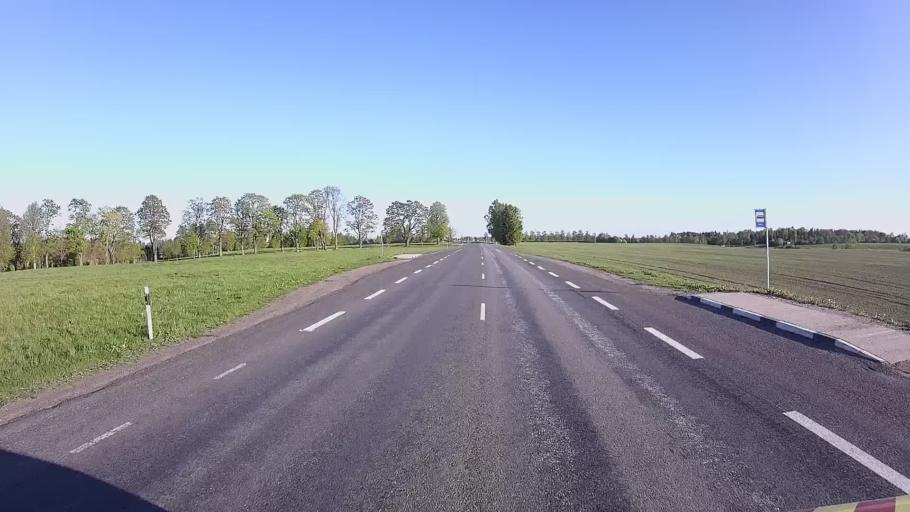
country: EE
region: Viljandimaa
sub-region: Viljandi linn
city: Viljandi
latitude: 58.3966
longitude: 25.5918
